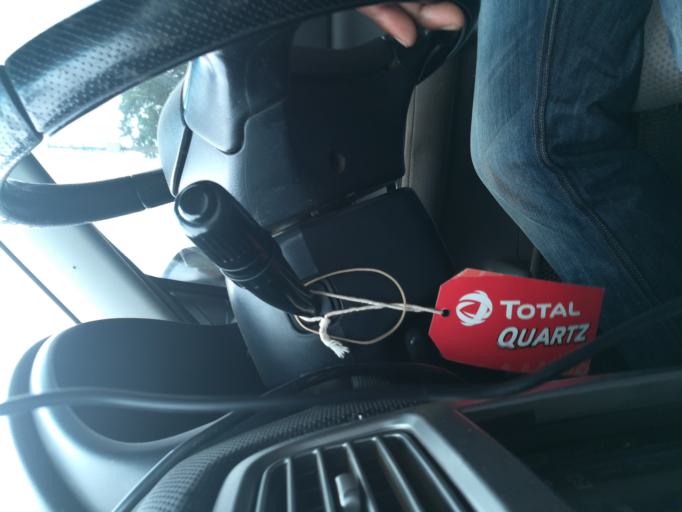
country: KE
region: Nairobi Area
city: Thika
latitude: -1.0422
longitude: 37.0708
